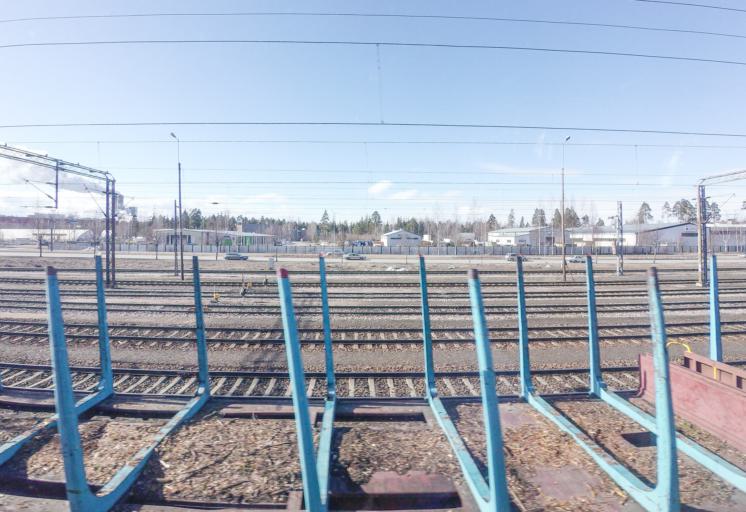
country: FI
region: South Karelia
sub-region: Lappeenranta
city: Lappeenranta
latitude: 61.0664
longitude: 28.2599
